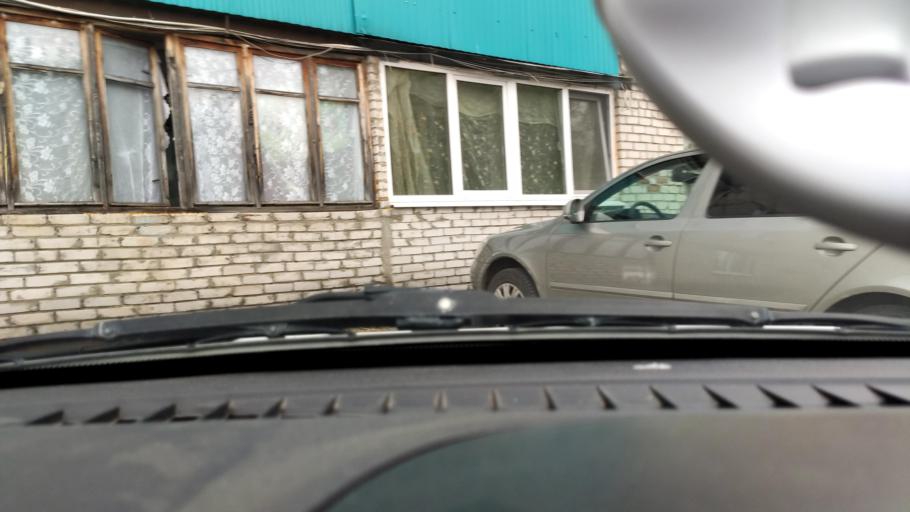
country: RU
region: Perm
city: Ferma
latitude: 57.8927
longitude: 56.2953
